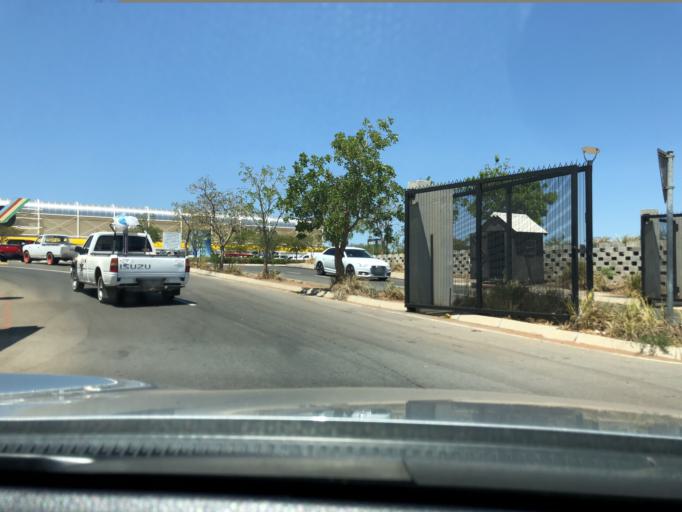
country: ZA
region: Limpopo
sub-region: Capricorn District Municipality
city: Polokwane
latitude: -23.8744
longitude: 29.4637
